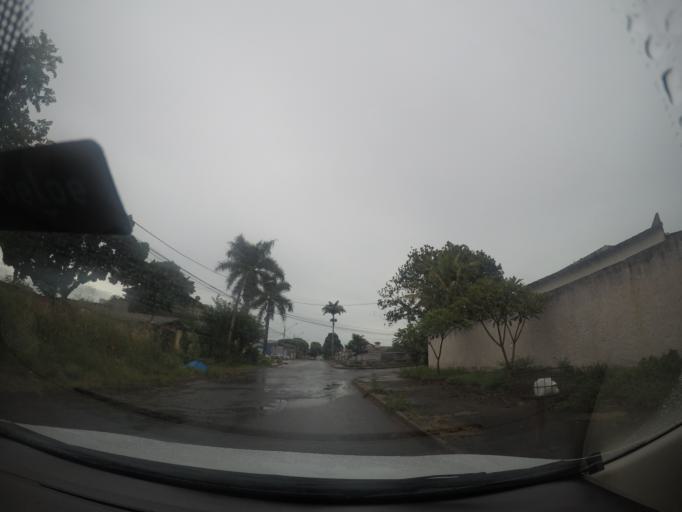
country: BR
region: Goias
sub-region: Goiania
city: Goiania
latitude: -16.6347
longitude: -49.2333
